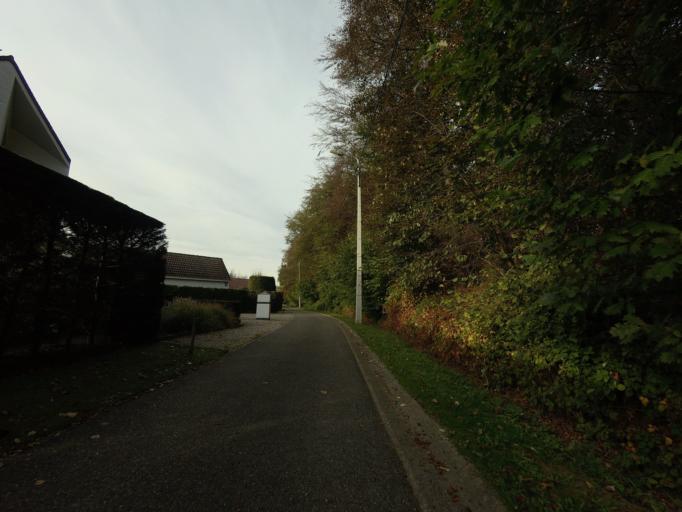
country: BE
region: Flanders
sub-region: Provincie Vlaams-Brabant
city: Kortenberg
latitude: 50.8959
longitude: 4.5919
